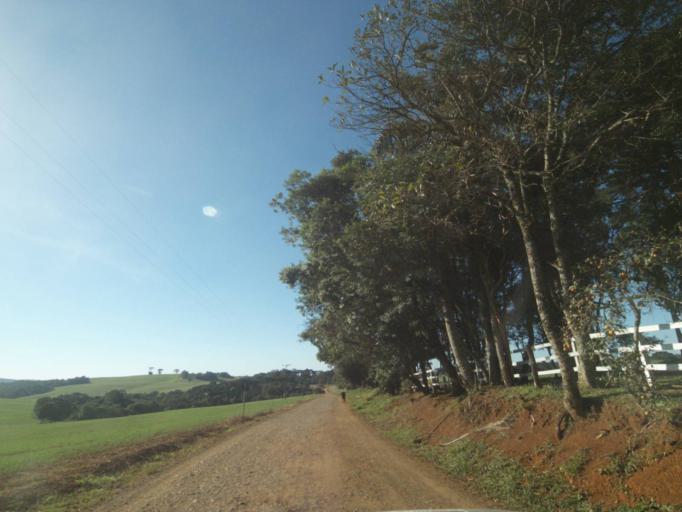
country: BR
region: Parana
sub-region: Tibagi
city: Tibagi
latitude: -24.5404
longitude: -50.4982
